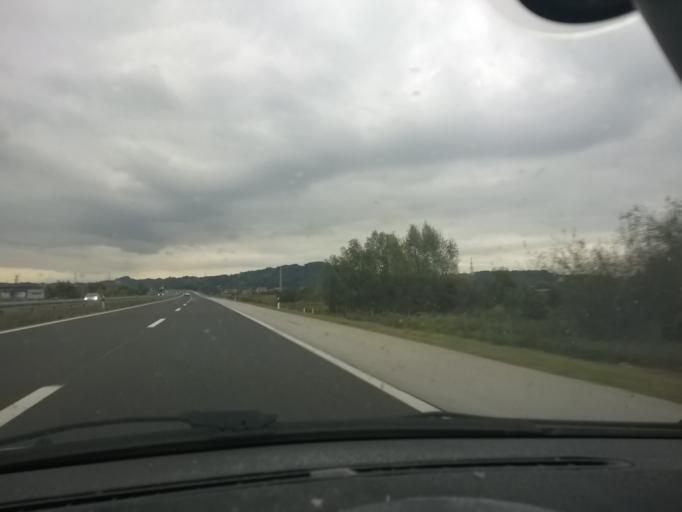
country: HR
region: Krapinsko-Zagorska
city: Zabok
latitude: 46.0201
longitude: 15.9050
